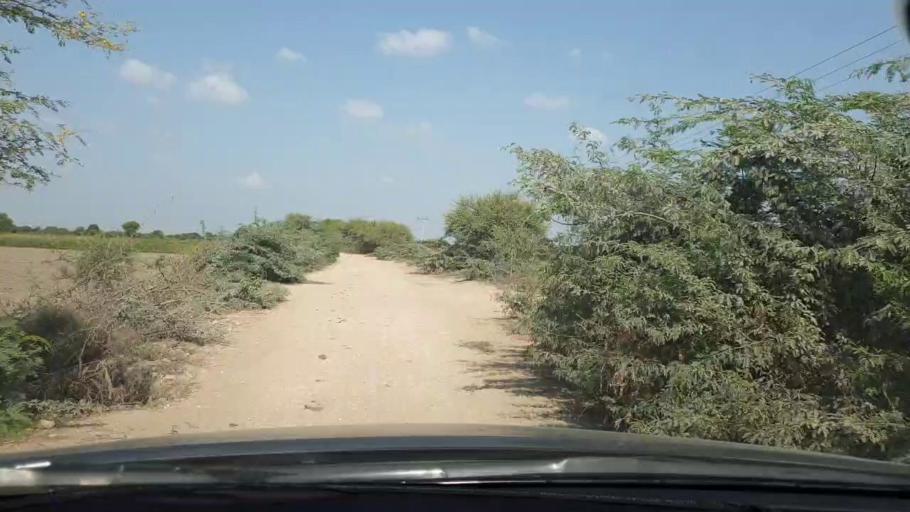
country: PK
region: Sindh
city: Naukot
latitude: 24.8772
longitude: 69.2615
